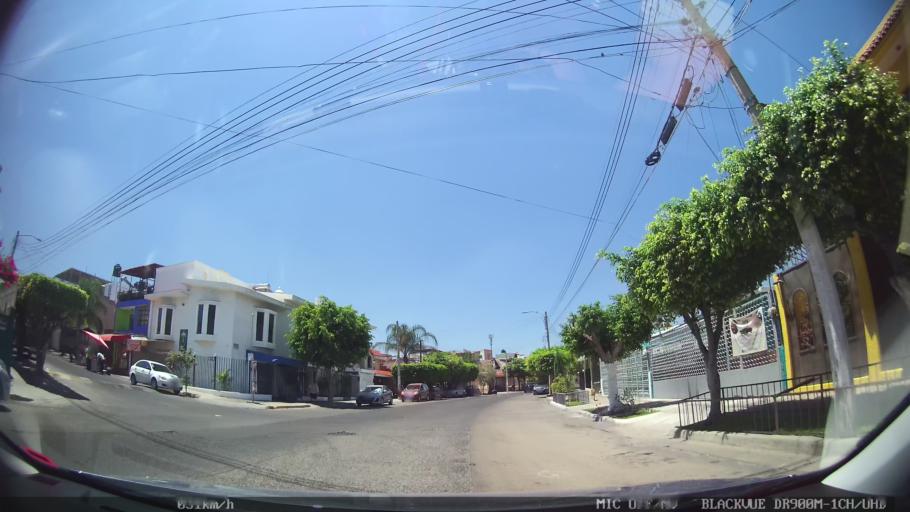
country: MX
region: Jalisco
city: Tlaquepaque
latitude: 20.6814
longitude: -103.2876
